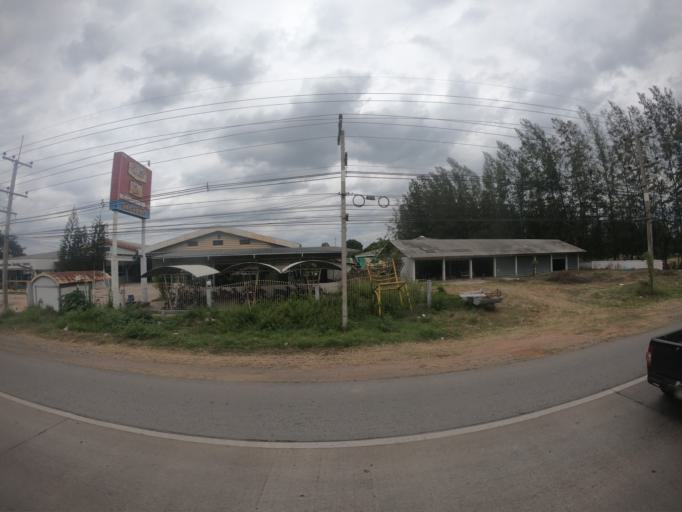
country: TH
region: Nakhon Ratchasima
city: Chok Chai
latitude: 14.7902
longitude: 102.1675
